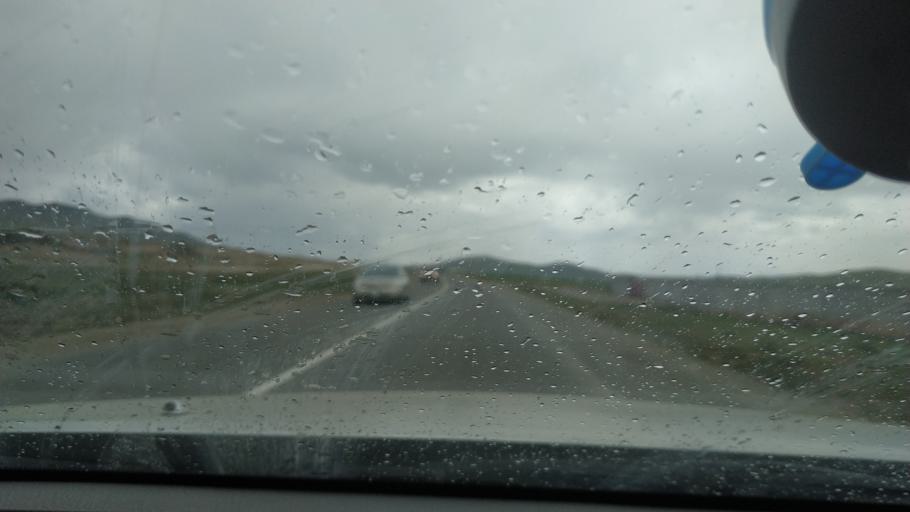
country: MN
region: Ulaanbaatar
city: Ulaanbaatar
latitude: 47.8158
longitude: 106.7558
